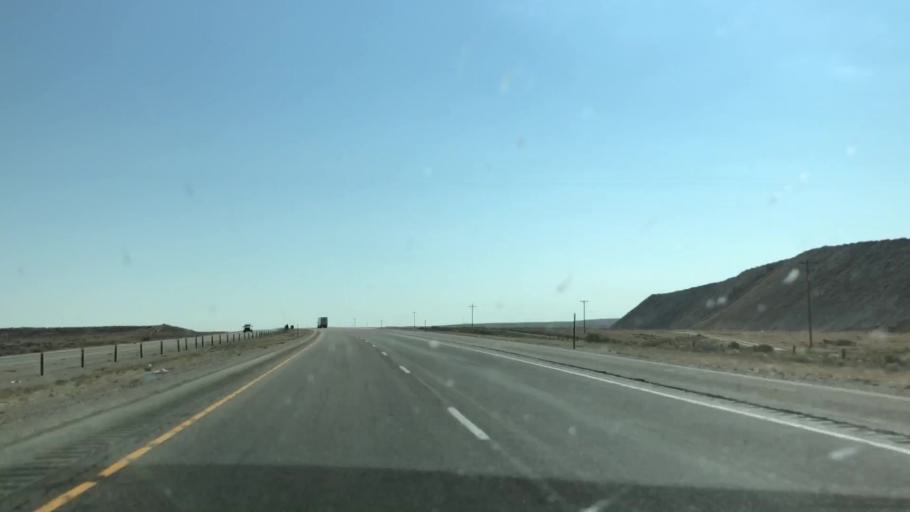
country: US
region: Wyoming
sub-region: Sweetwater County
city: Rock Springs
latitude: 41.6466
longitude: -108.6537
